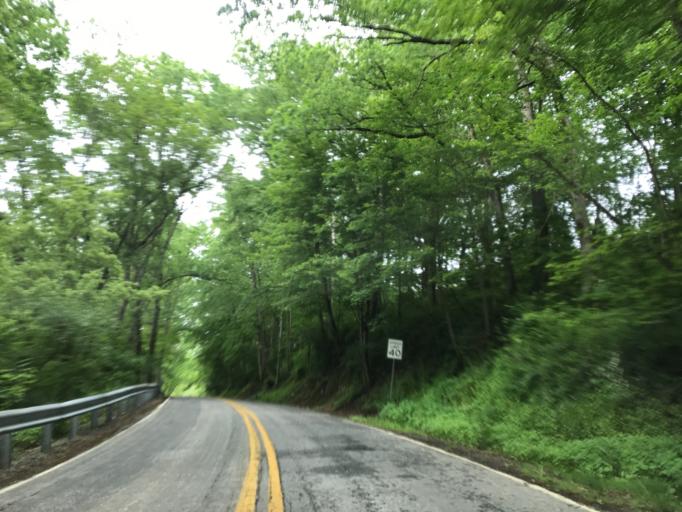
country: US
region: Pennsylvania
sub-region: York County
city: Susquehanna Trails
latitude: 39.7742
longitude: -76.4233
